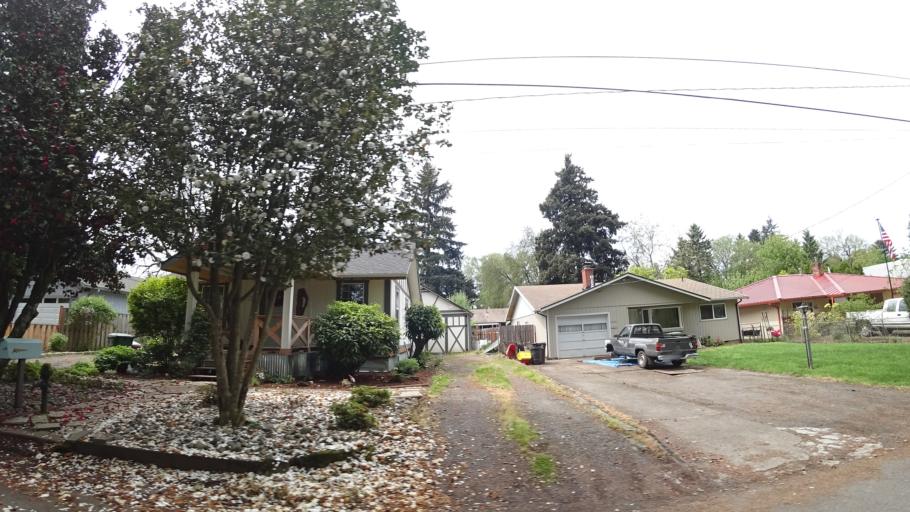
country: US
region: Oregon
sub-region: Clackamas County
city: Milwaukie
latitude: 45.4533
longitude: -122.6222
